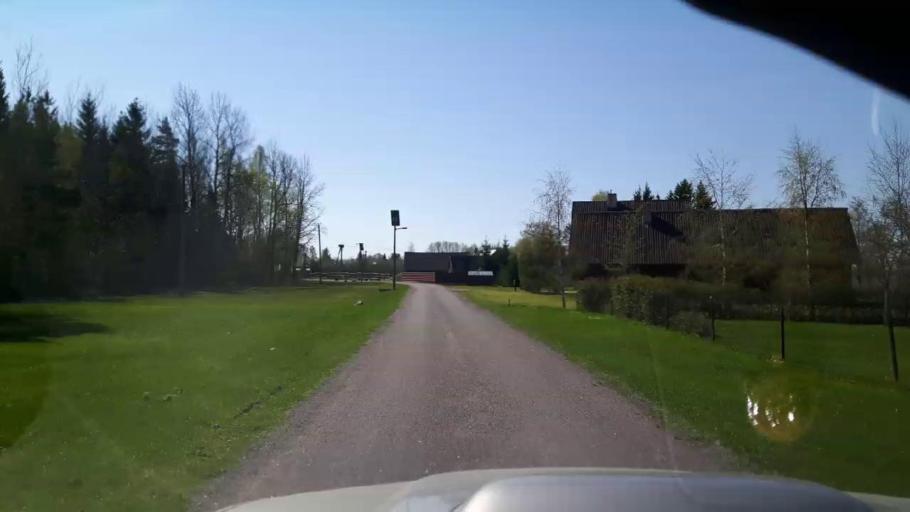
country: EE
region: Paernumaa
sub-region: Tootsi vald
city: Tootsi
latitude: 58.4700
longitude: 24.7872
